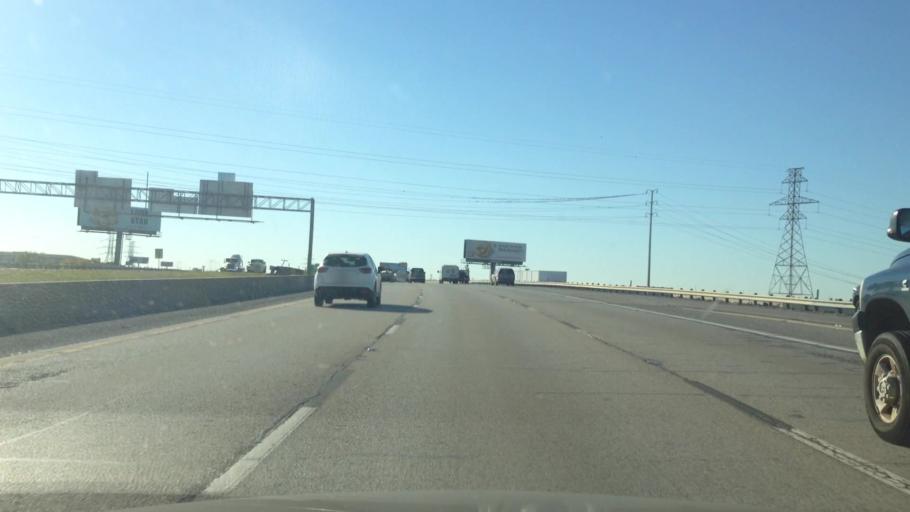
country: US
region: Texas
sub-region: Tarrant County
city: Blue Mound
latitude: 32.8430
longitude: -97.3454
